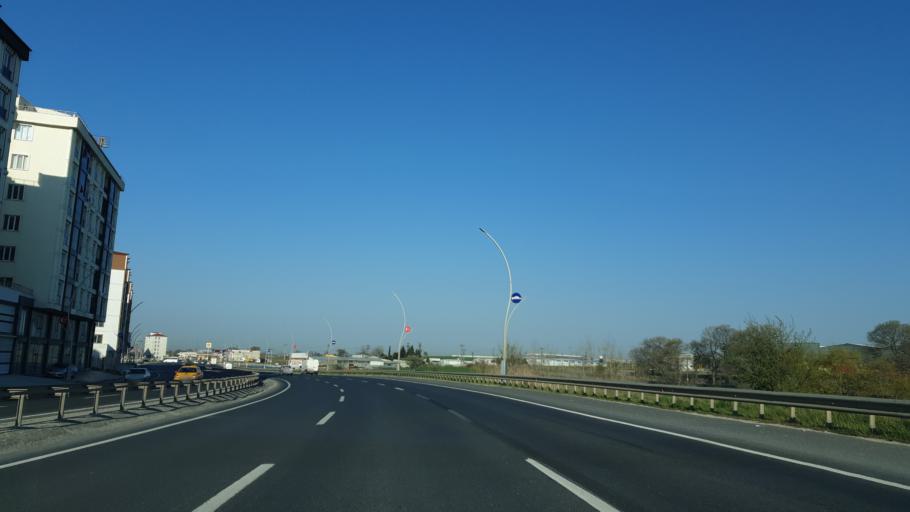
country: TR
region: Tekirdag
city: Cerkezkoey
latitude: 41.2731
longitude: 27.9690
